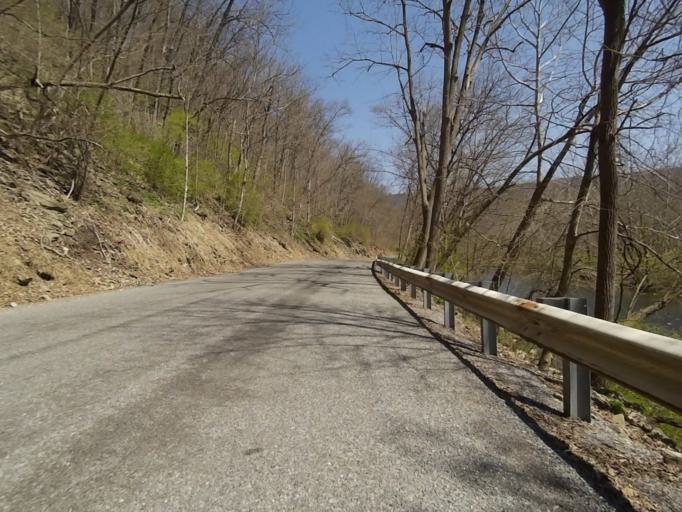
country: US
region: Pennsylvania
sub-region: Blair County
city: Williamsburg
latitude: 40.5245
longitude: -78.1752
